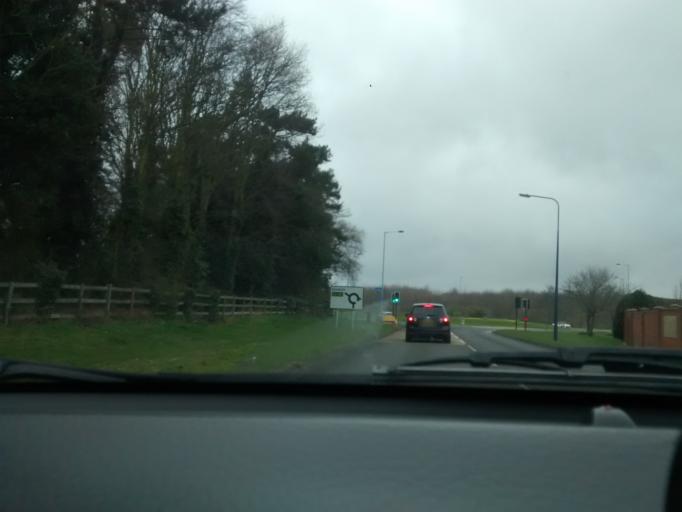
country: GB
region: England
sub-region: Suffolk
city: Felixstowe
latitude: 51.9707
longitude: 1.3473
